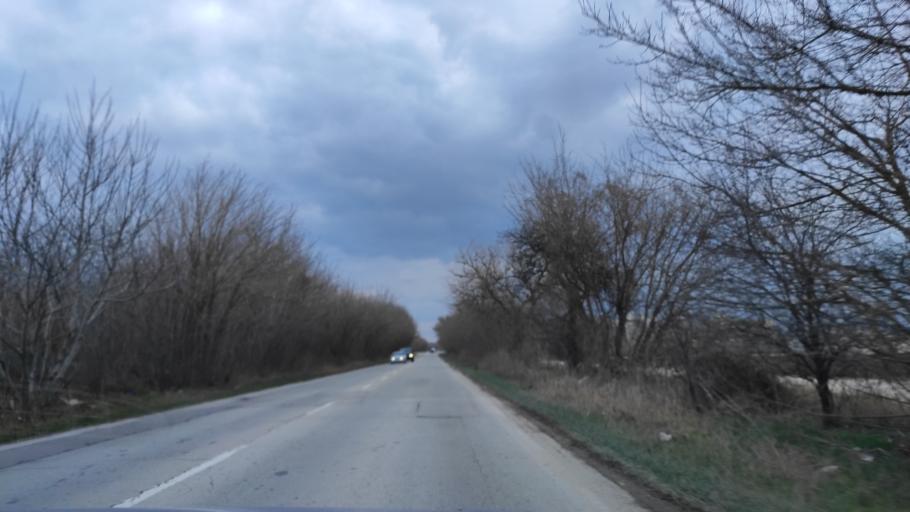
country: BG
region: Varna
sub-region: Obshtina Aksakovo
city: Aksakovo
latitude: 43.2285
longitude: 27.8386
